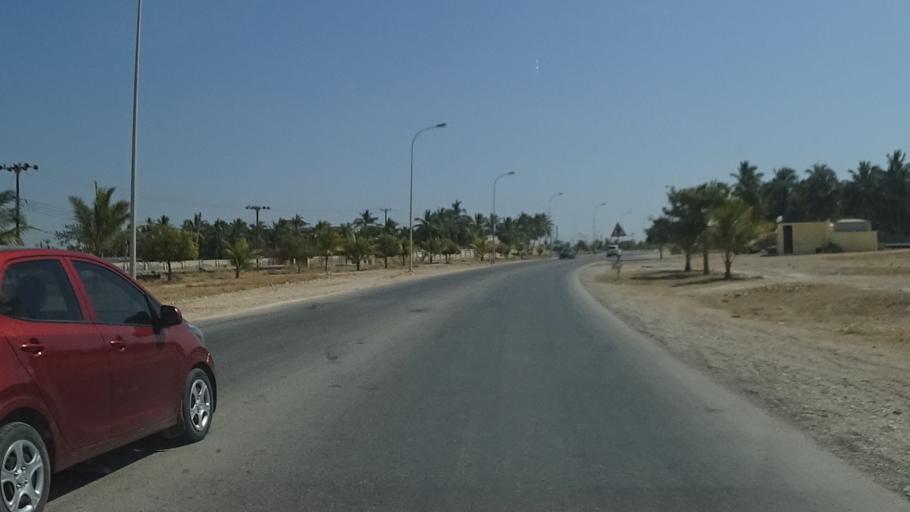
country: OM
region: Zufar
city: Salalah
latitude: 17.0410
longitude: 54.1712
